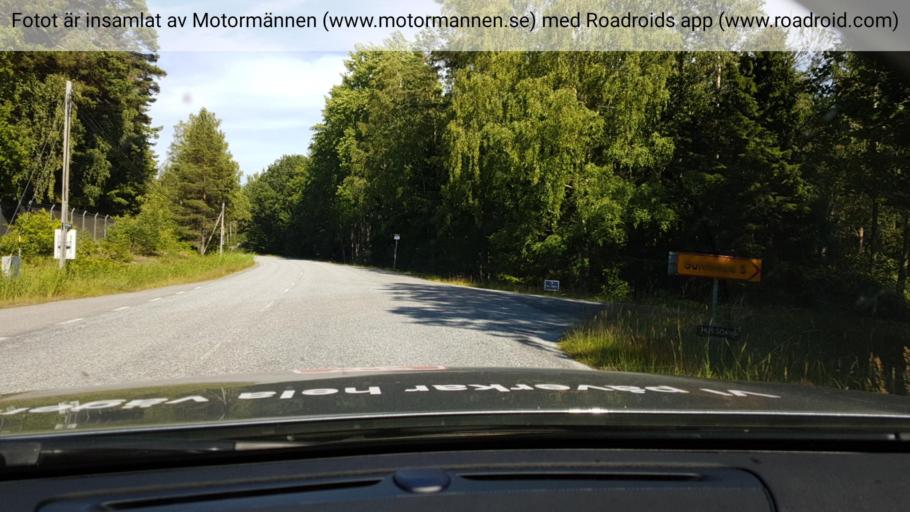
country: SE
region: Stockholm
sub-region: Nynashamns Kommun
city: Nynashamn
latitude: 58.9697
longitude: 18.0610
